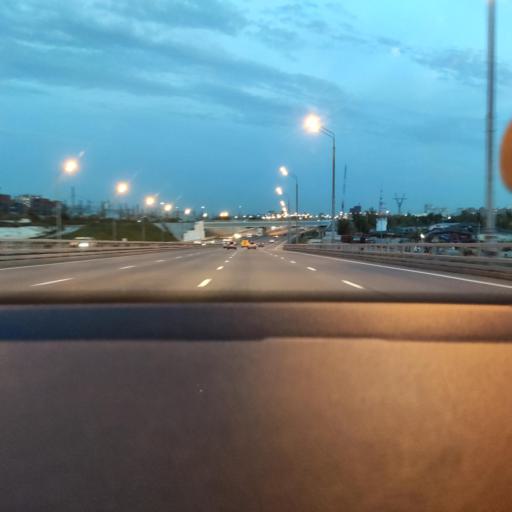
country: RU
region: Moscow
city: Zapadnoye Degunino
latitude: 55.8558
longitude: 37.5383
